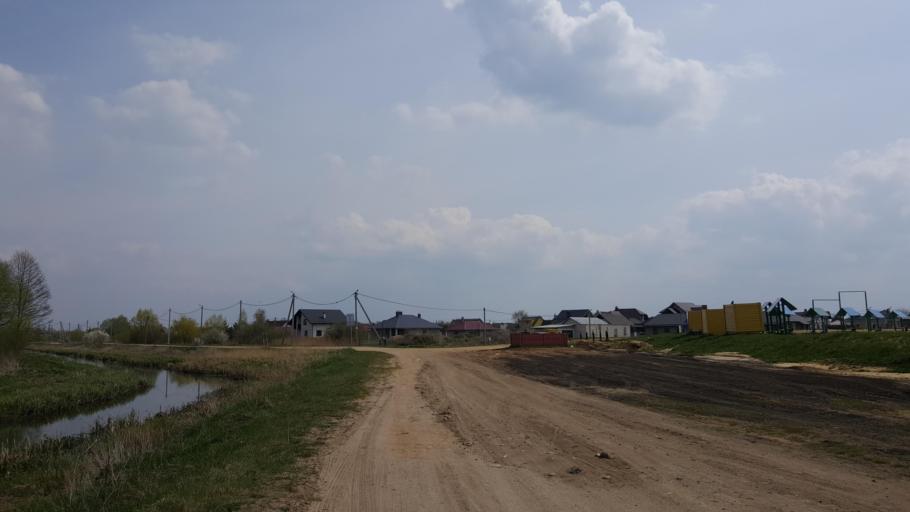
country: BY
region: Brest
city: Zhabinka
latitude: 52.2007
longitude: 23.9896
